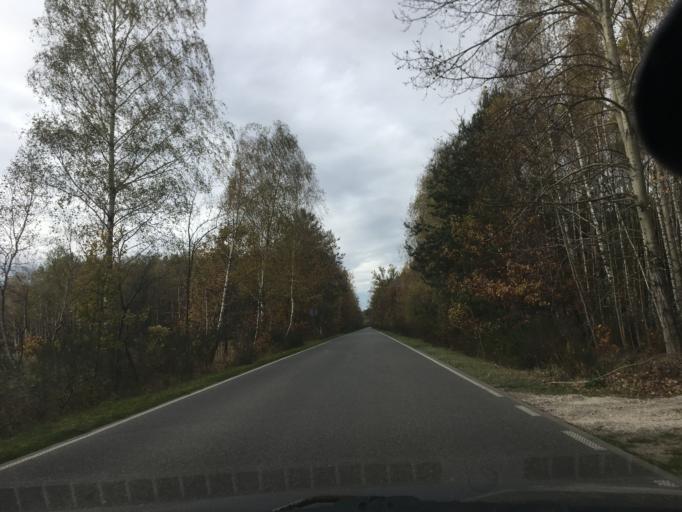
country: PL
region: Masovian Voivodeship
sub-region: Powiat zyrardowski
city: Radziejowice
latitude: 51.9671
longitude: 20.5985
